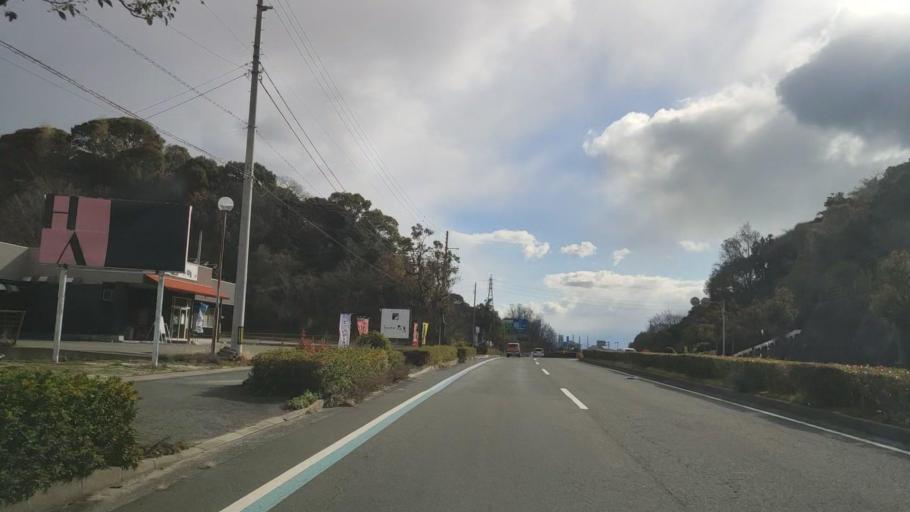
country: JP
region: Ehime
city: Hojo
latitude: 34.0576
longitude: 132.9728
